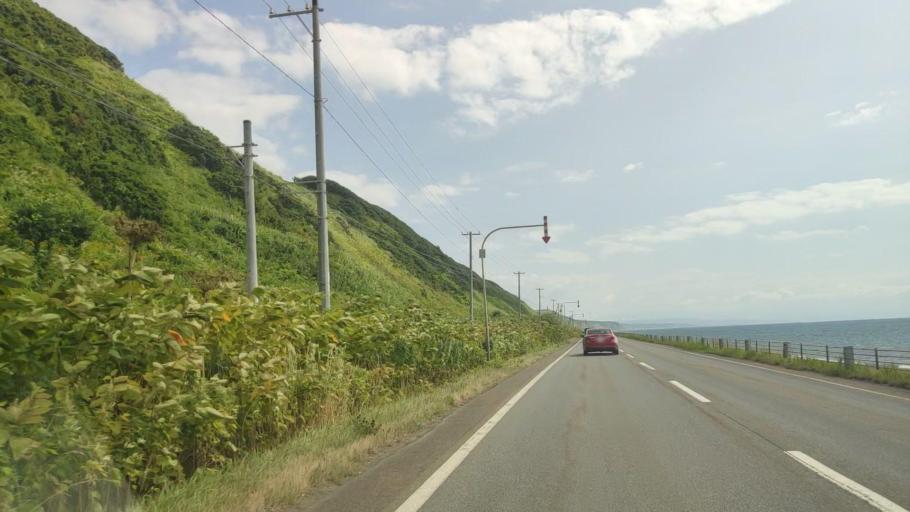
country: JP
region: Hokkaido
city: Rumoi
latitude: 44.0846
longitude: 141.6620
